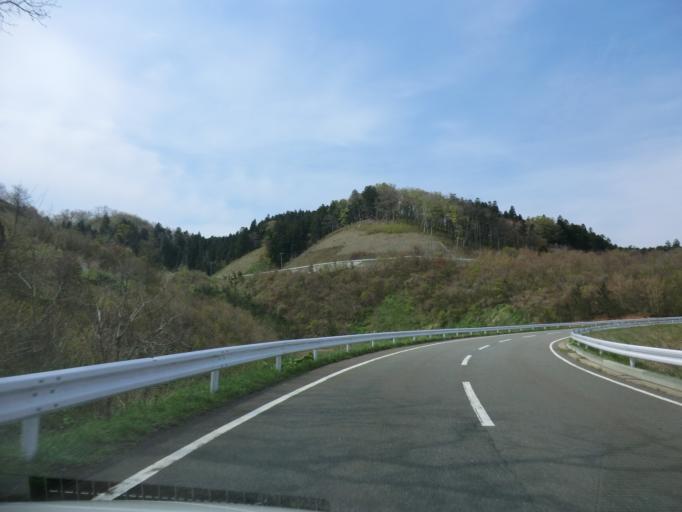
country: JP
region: Aomori
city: Mutsu
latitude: 41.3645
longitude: 140.8315
